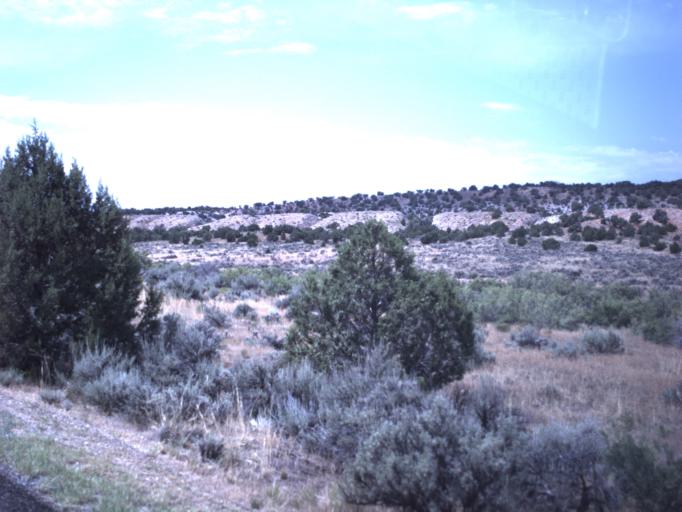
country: US
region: Utah
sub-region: Uintah County
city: Maeser
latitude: 40.5315
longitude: -109.5335
